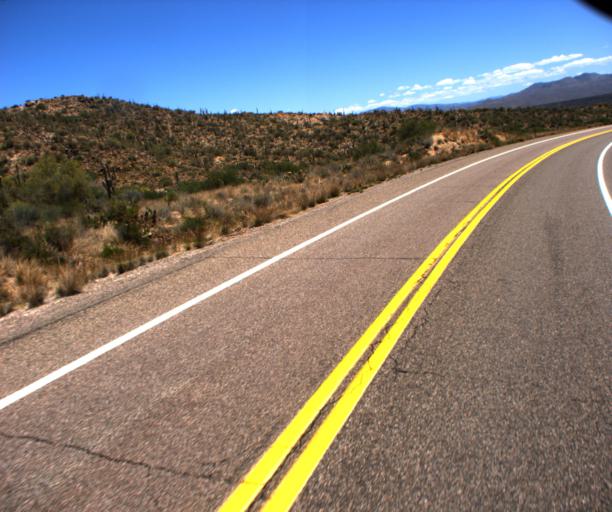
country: US
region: Arizona
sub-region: Yavapai County
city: Bagdad
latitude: 34.5248
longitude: -113.1176
